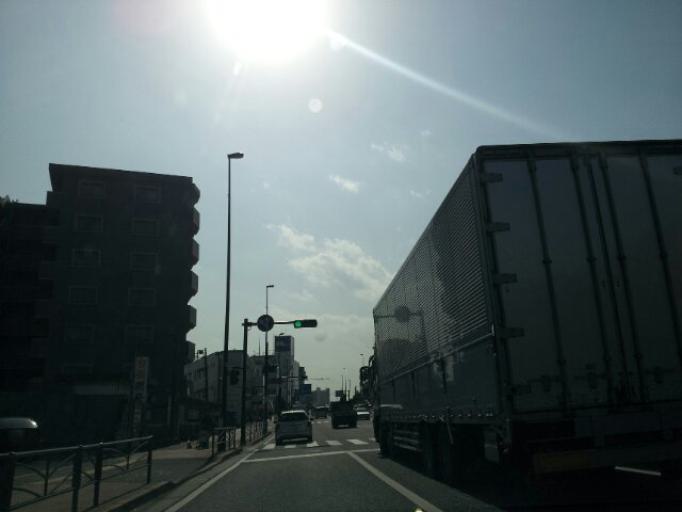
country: JP
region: Kanagawa
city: Yokohama
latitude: 35.4864
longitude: 139.6441
